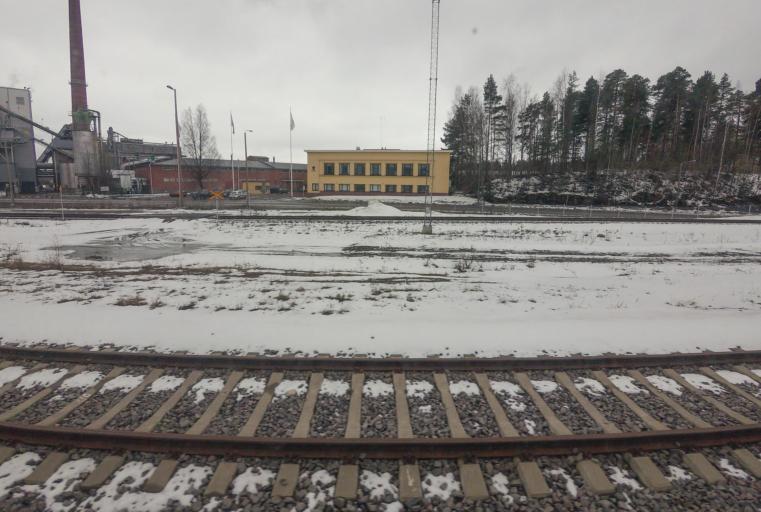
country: FI
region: Southern Savonia
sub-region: Savonlinna
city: Savonlinna
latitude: 61.8630
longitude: 28.9194
